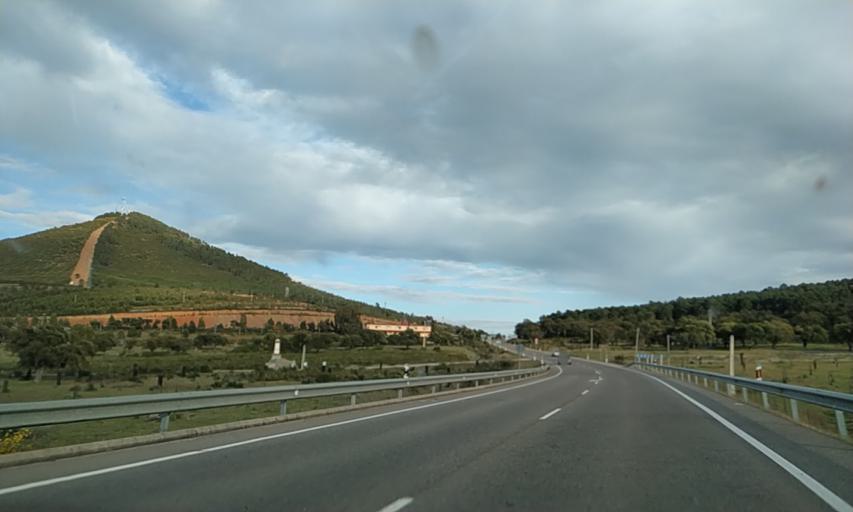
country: ES
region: Extremadura
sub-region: Provincia de Caceres
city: Canaveral
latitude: 39.8230
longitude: -6.3704
